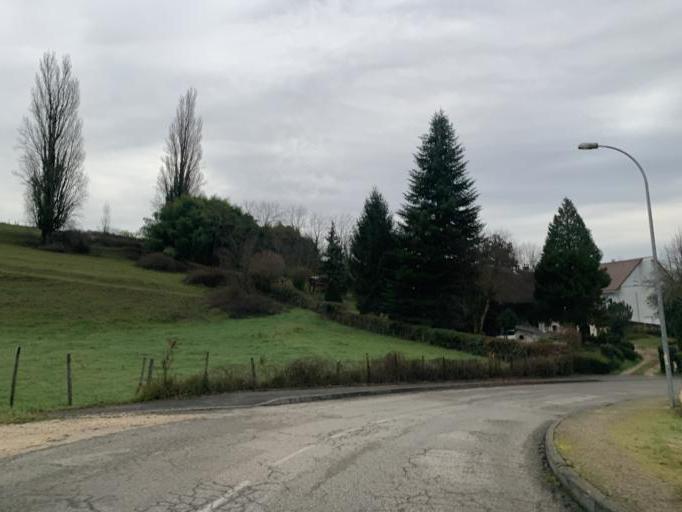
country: FR
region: Rhone-Alpes
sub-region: Departement de l'Ain
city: Belley
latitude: 45.7669
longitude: 5.6920
